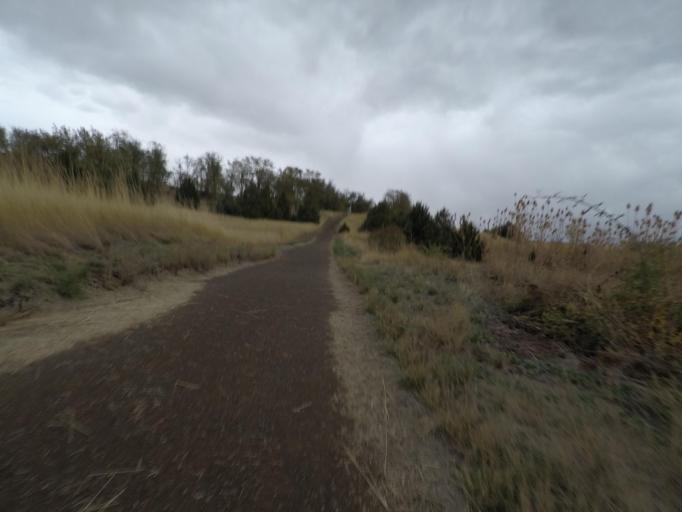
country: US
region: Washington
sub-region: Walla Walla County
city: Walla Walla East
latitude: 46.0641
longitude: -118.2563
